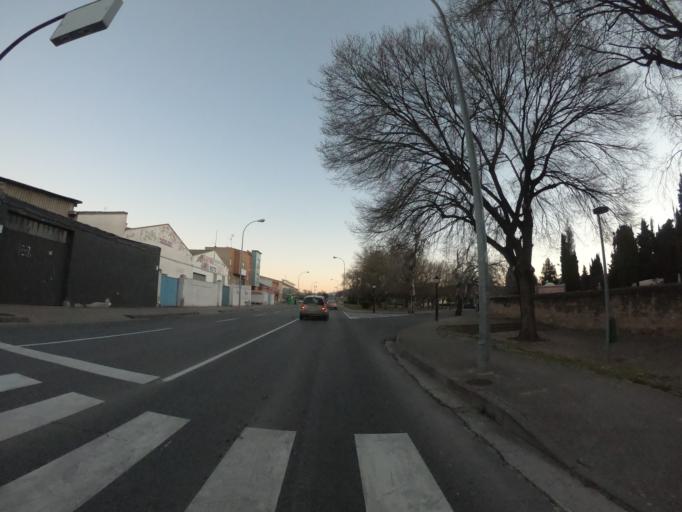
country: ES
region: La Rioja
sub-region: Provincia de La Rioja
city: Logrono
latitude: 42.4738
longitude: -2.4447
